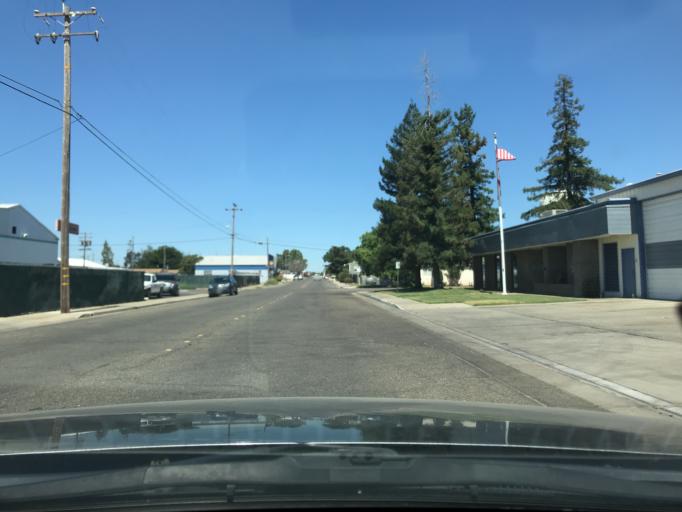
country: US
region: California
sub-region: Merced County
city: Atwater
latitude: 37.3447
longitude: -120.6029
